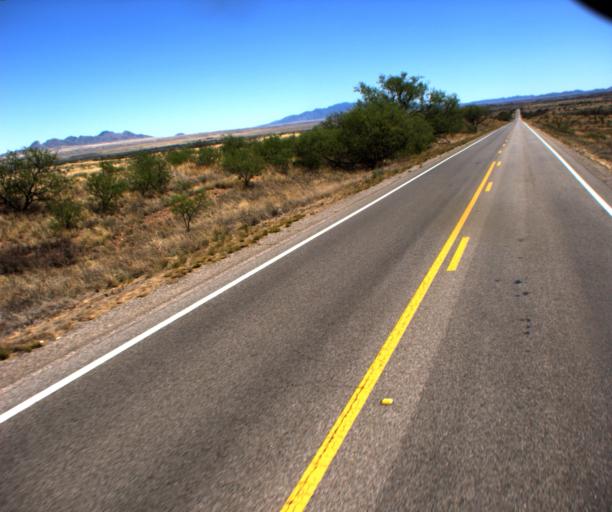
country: US
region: Arizona
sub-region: Pima County
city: Corona de Tucson
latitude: 31.7637
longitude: -110.6796
